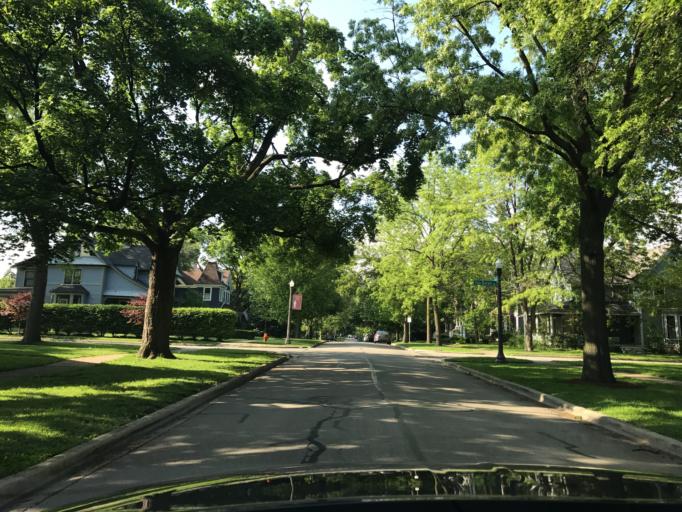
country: US
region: Illinois
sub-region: DuPage County
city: Naperville
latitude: 41.7733
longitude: -88.1409
